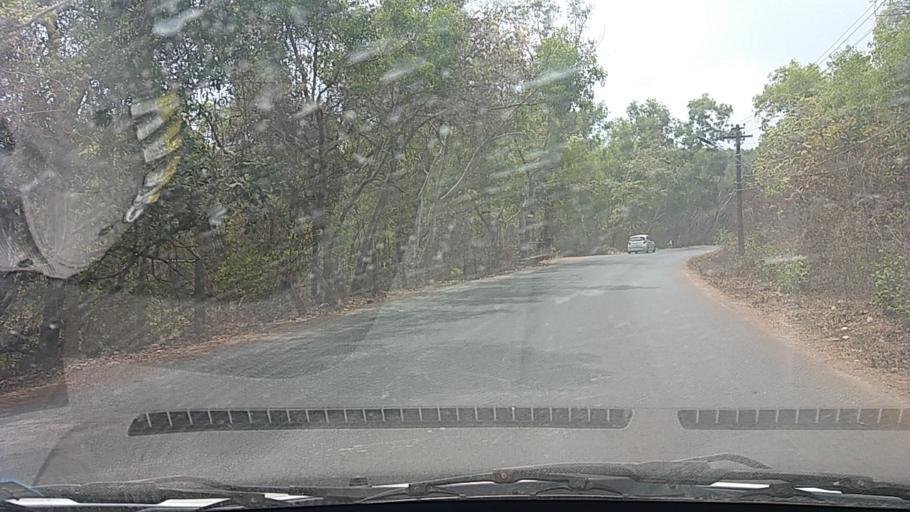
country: IN
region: Goa
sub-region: North Goa
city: Saligao
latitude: 15.5382
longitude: 73.7937
